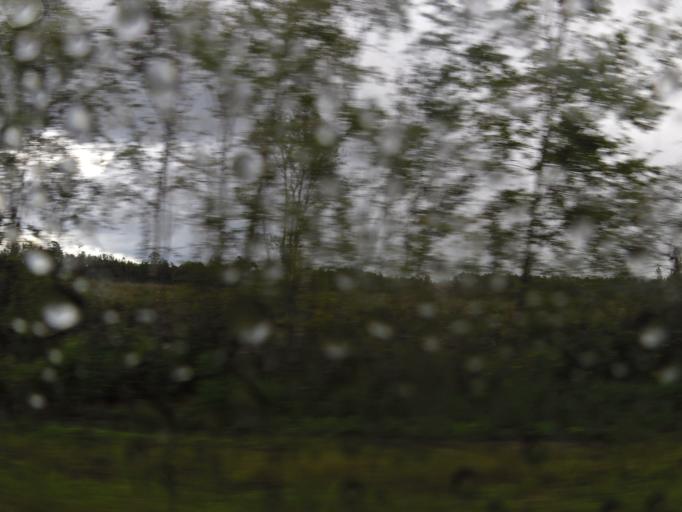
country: US
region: Florida
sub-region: Nassau County
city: Hilliard
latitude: 30.5495
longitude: -82.0410
